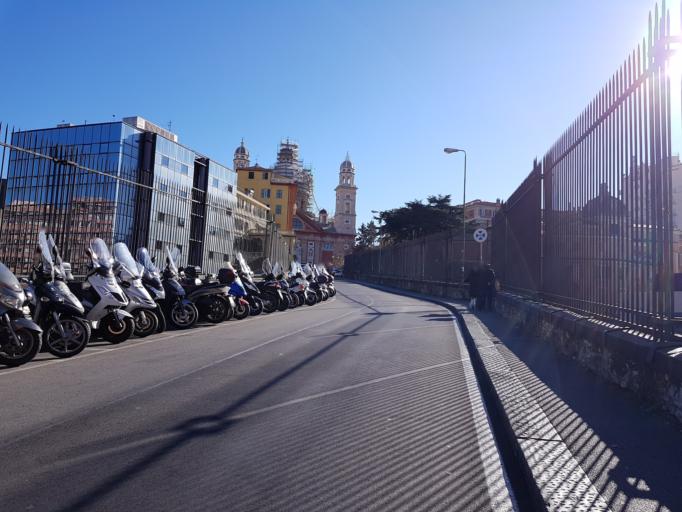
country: IT
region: Liguria
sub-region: Provincia di Genova
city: San Teodoro
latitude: 44.4035
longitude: 8.9329
